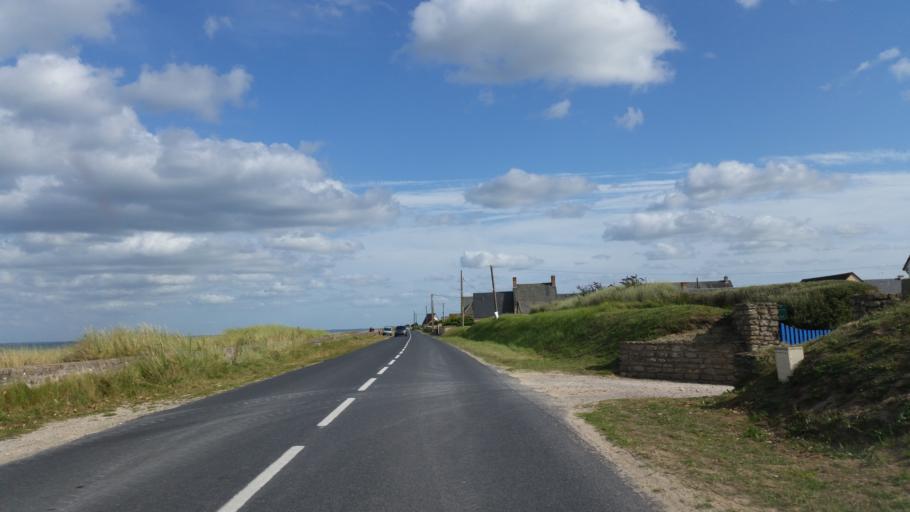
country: FR
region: Lower Normandy
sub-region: Departement de la Manche
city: Sainte-Mere-Eglise
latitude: 49.4570
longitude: -1.2246
